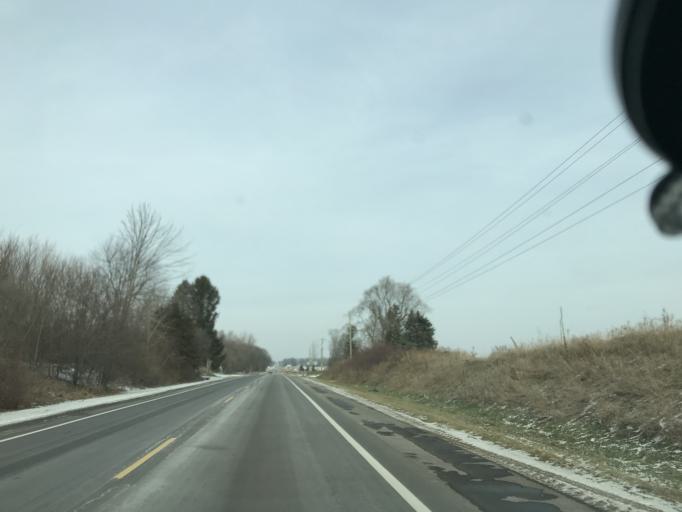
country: US
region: Michigan
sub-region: Ionia County
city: Lake Odessa
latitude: 42.7914
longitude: -85.0744
